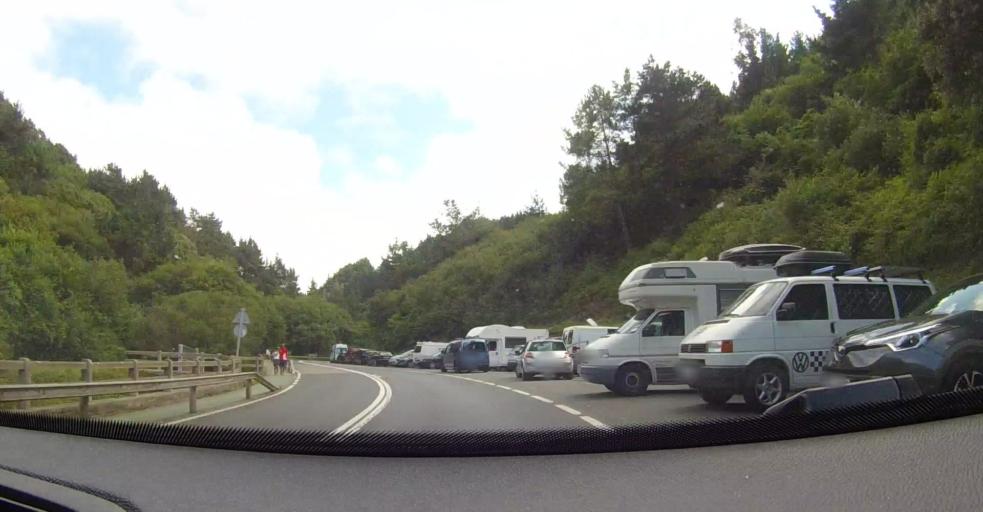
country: ES
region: Basque Country
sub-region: Bizkaia
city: Elantxobe
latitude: 43.4066
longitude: -2.6535
